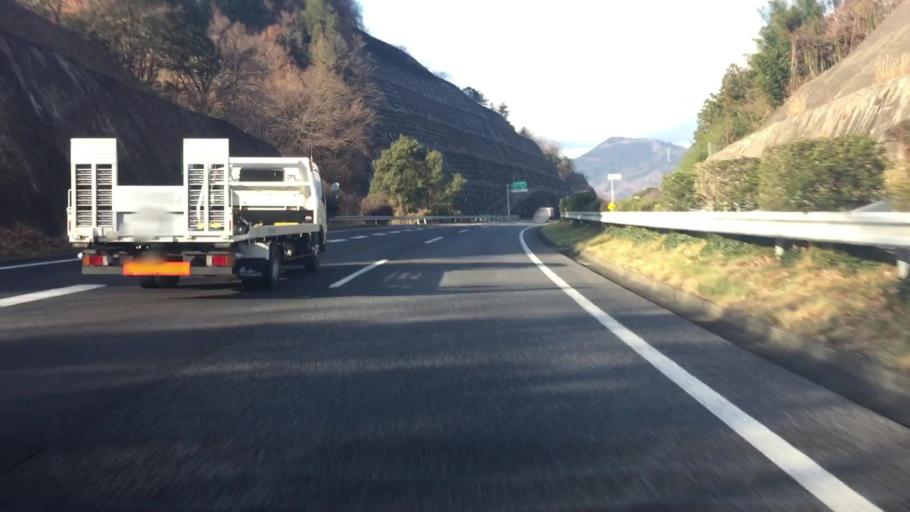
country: JP
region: Gunma
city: Tomioka
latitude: 36.2376
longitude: 138.8514
